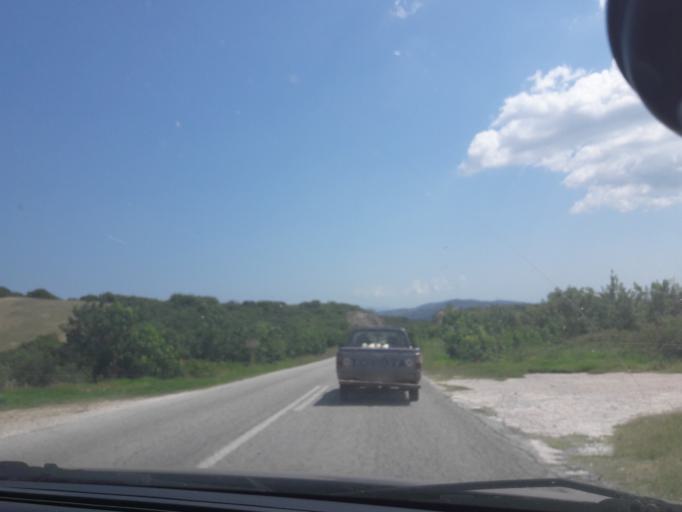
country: GR
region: Central Macedonia
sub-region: Nomos Chalkidikis
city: Ormylia
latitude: 40.3594
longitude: 23.5807
